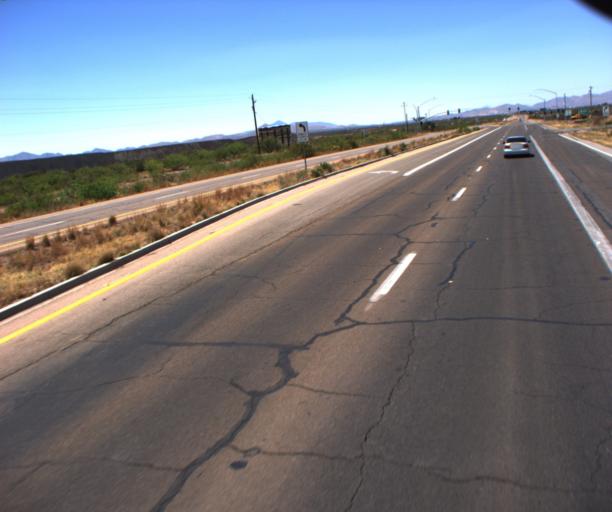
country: US
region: Arizona
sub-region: Cochise County
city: Pirtleville
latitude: 31.3522
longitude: -109.5770
